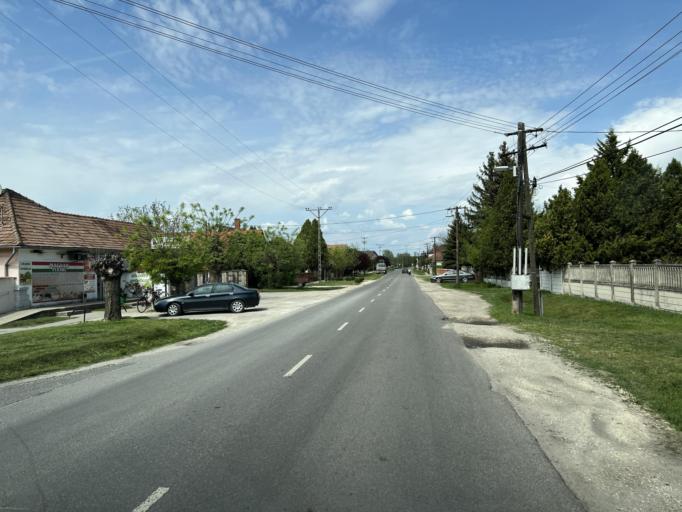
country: HU
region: Pest
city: Albertirsa
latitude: 47.2307
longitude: 19.6120
